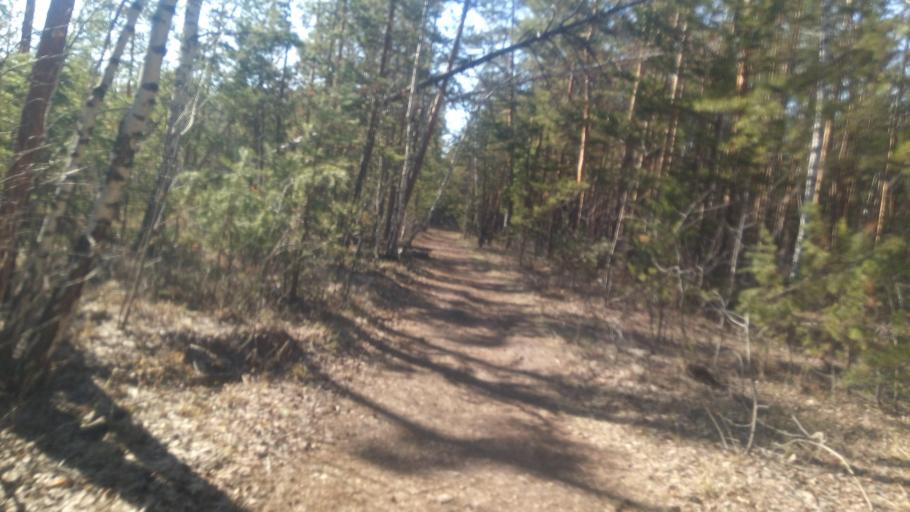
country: RU
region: Chelyabinsk
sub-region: Gorod Chelyabinsk
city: Chelyabinsk
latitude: 55.1601
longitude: 61.3346
